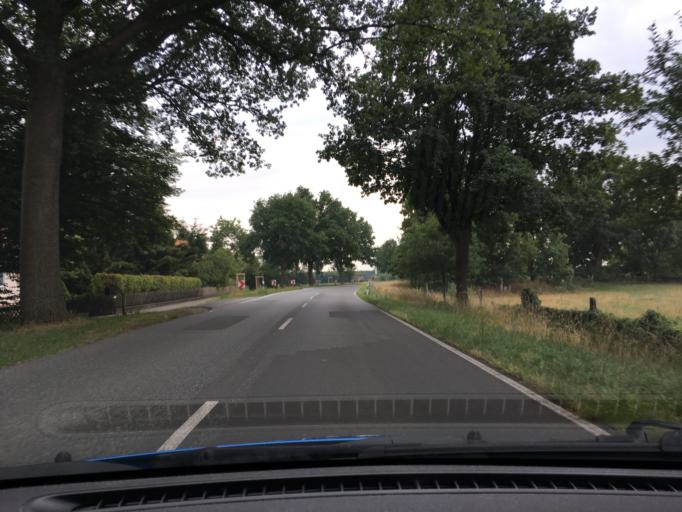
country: DE
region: Lower Saxony
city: Adelheidsdorf
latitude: 52.5427
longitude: 10.0528
